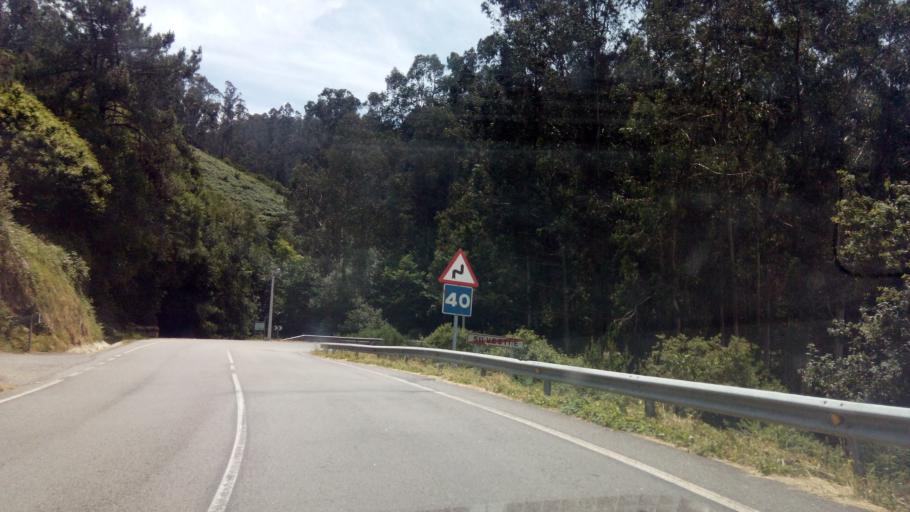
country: ES
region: Galicia
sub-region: Provincia de Pontevedra
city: Marin
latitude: 42.3500
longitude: -8.6978
